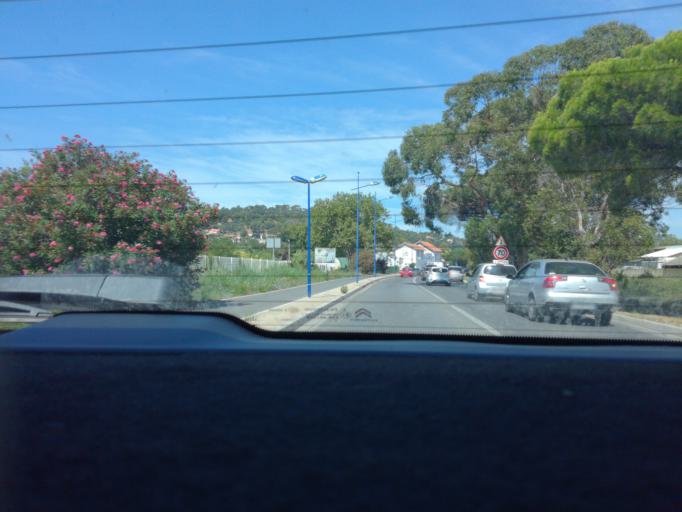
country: FR
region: Provence-Alpes-Cote d'Azur
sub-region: Departement du Var
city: Hyeres
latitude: 43.0942
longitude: 6.1379
